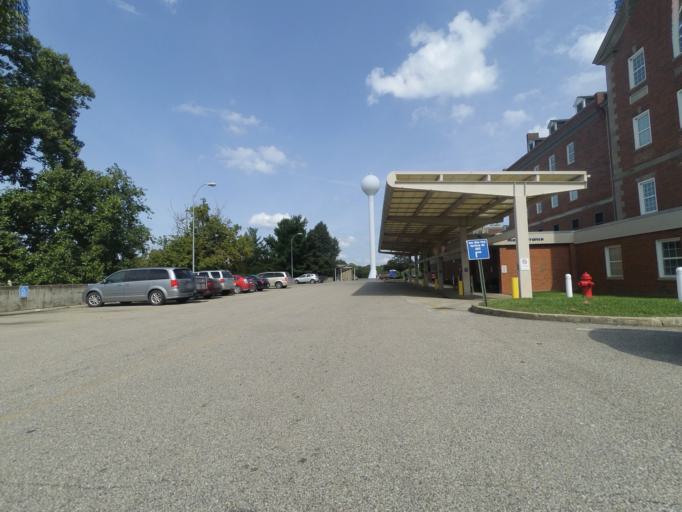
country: US
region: Ohio
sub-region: Lawrence County
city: Burlington
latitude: 38.3771
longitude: -82.5173
